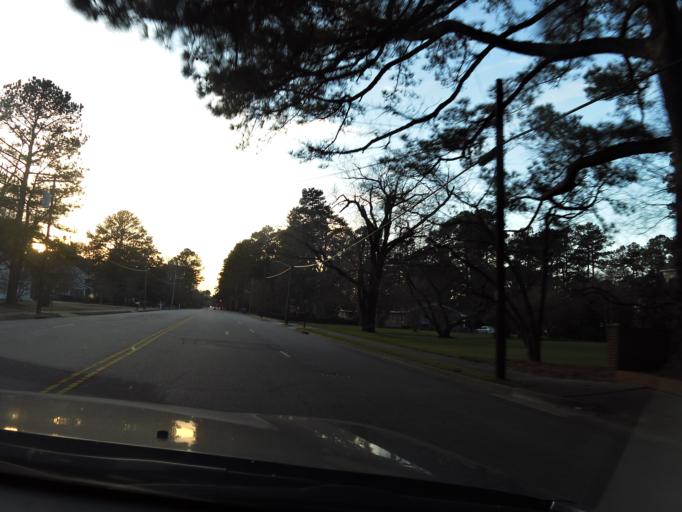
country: US
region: Virginia
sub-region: City of Franklin
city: Franklin
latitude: 36.6837
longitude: -76.9430
